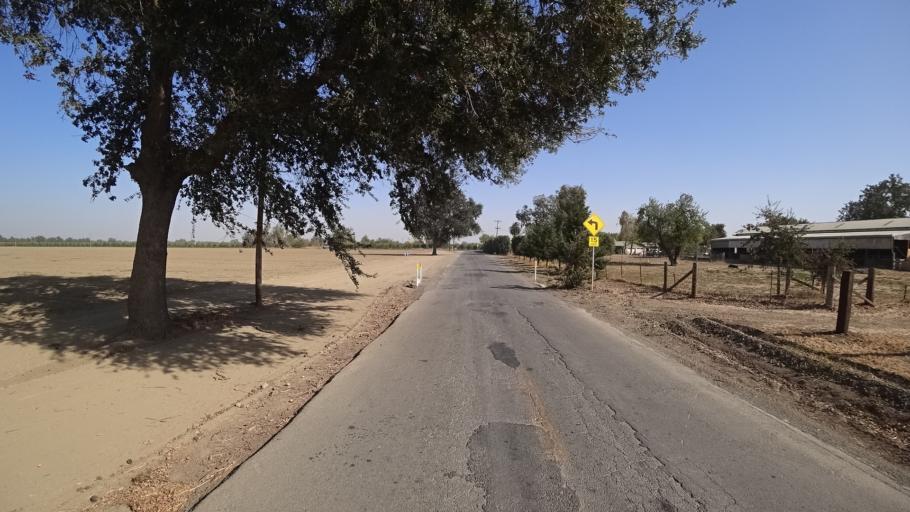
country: US
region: California
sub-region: Yolo County
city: Woodland
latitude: 38.7284
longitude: -121.8512
